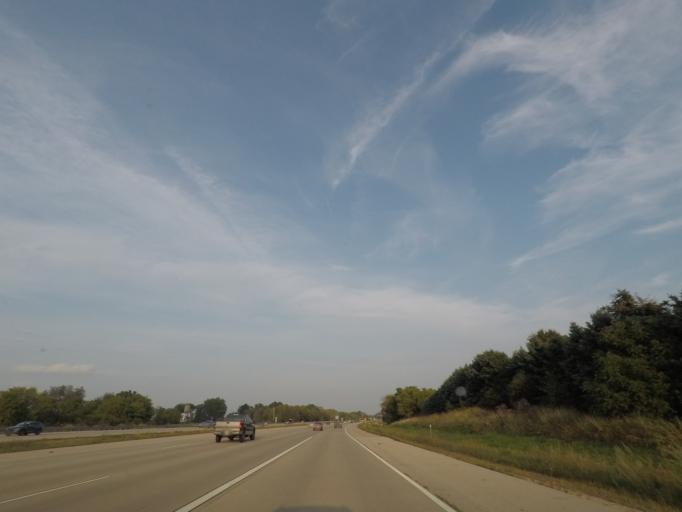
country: US
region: Wisconsin
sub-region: Dane County
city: Cottage Grove
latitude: 43.1100
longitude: -89.1935
